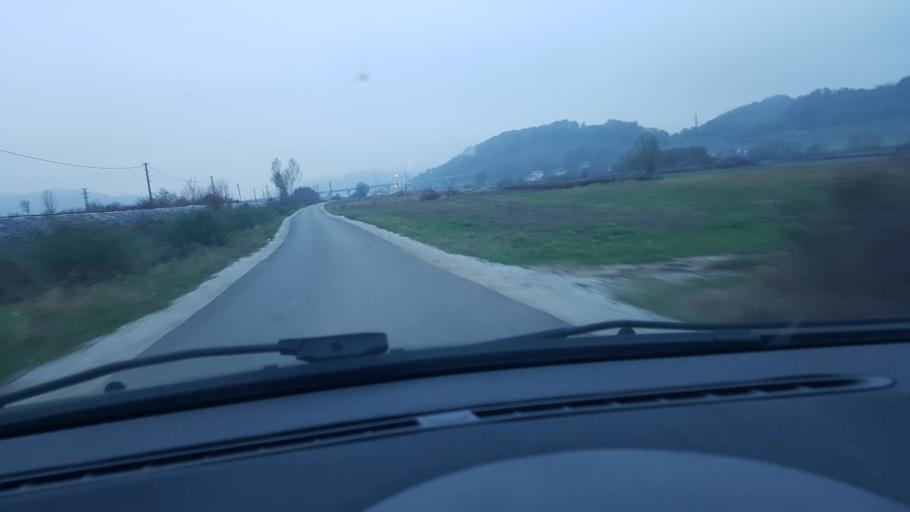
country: HR
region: Krapinsko-Zagorska
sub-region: Grad Krapina
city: Krapina
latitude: 46.1418
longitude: 15.8759
